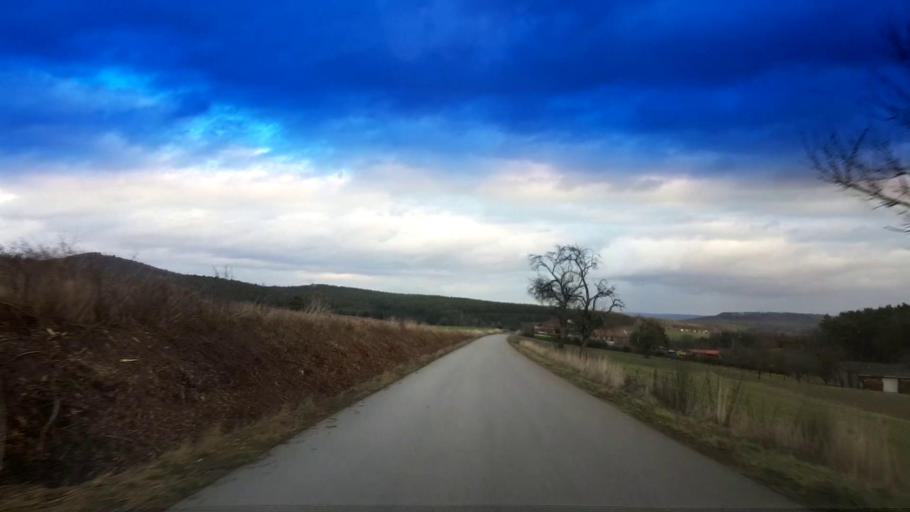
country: DE
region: Bavaria
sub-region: Upper Franconia
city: Lauter
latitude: 49.9799
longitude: 10.7606
